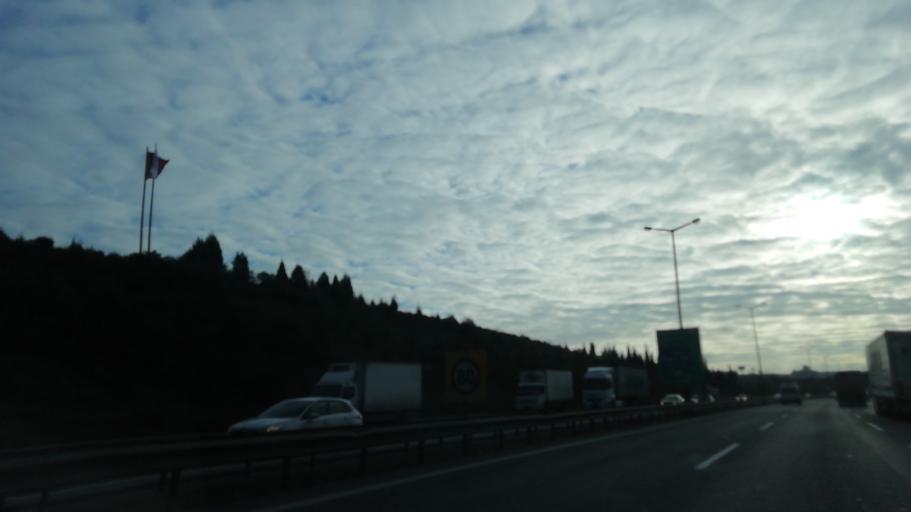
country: TR
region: Kocaeli
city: Balcik
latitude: 40.8749
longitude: 29.3905
